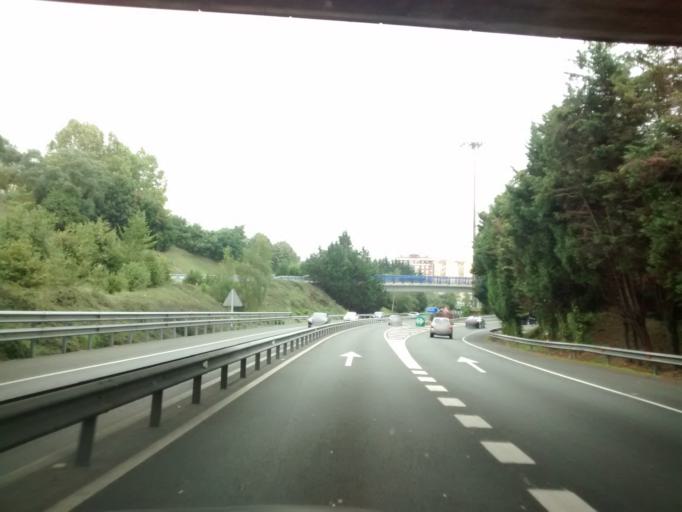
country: ES
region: Cantabria
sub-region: Provincia de Cantabria
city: Torrelavega
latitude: 43.3591
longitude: -4.0447
